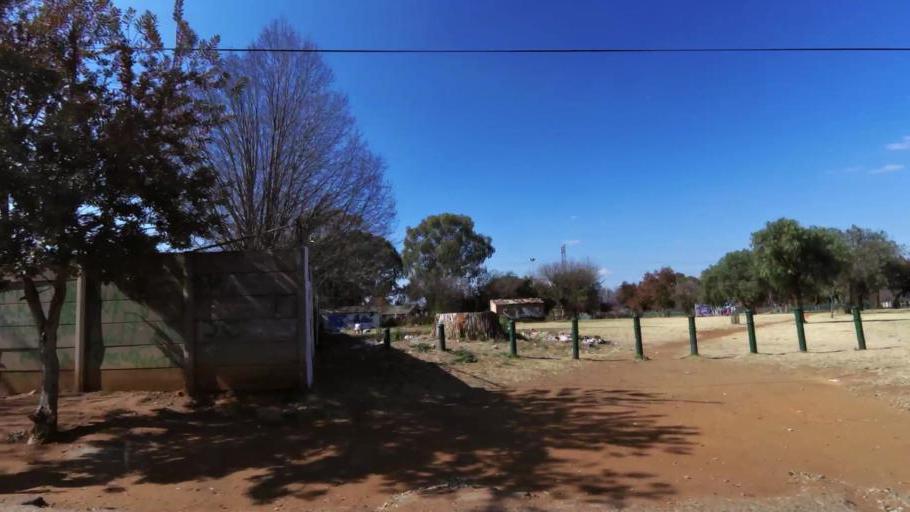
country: ZA
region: Gauteng
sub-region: City of Johannesburg Metropolitan Municipality
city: Soweto
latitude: -26.2415
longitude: 27.8864
